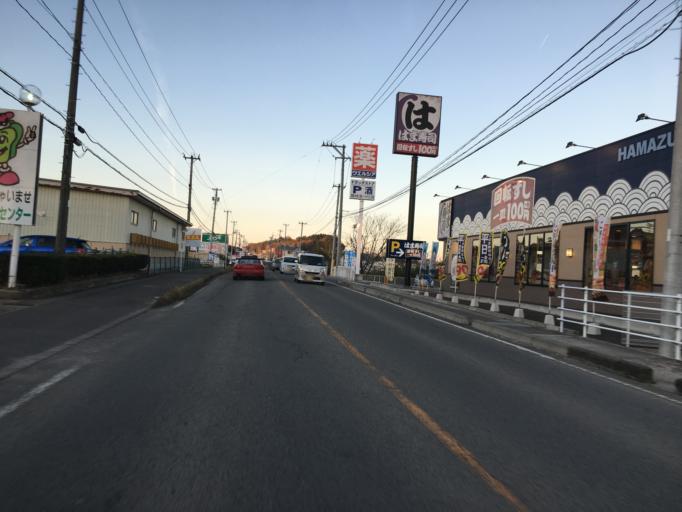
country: JP
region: Fukushima
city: Nihommatsu
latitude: 37.6083
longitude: 140.4607
